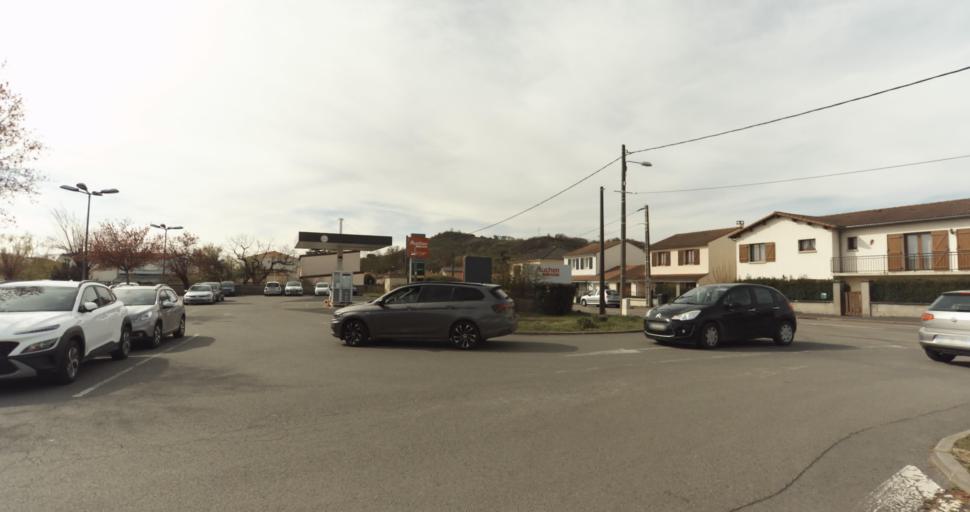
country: FR
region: Auvergne
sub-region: Departement du Puy-de-Dome
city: Cebazat
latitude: 45.8340
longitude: 3.0963
